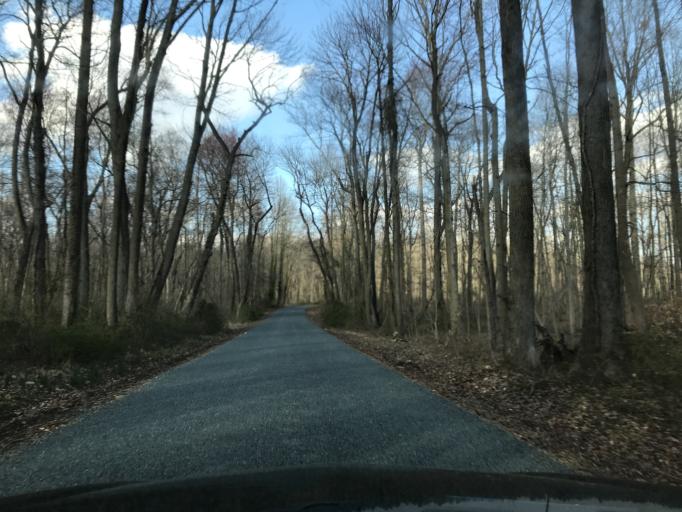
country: US
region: Maryland
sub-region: Harford County
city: Riverside
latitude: 39.4459
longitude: -76.2323
